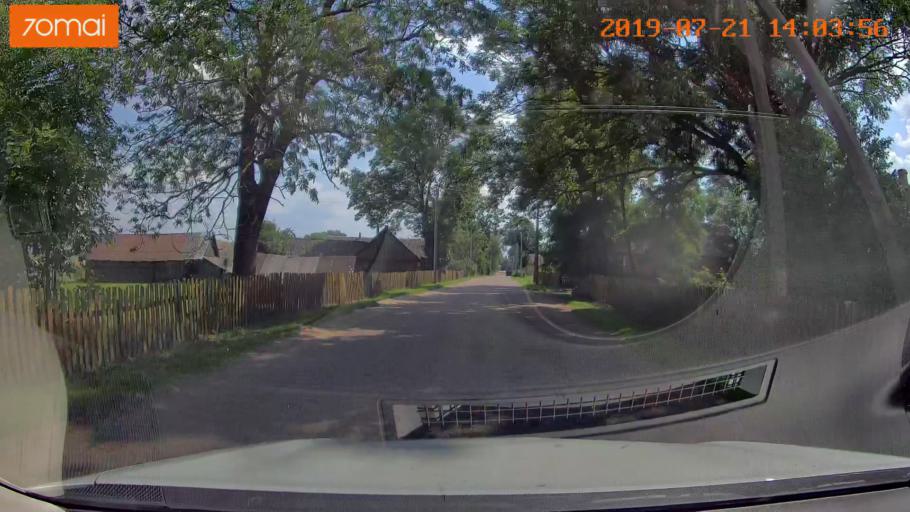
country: BY
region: Grodnenskaya
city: Lyubcha
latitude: 53.7250
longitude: 26.0950
